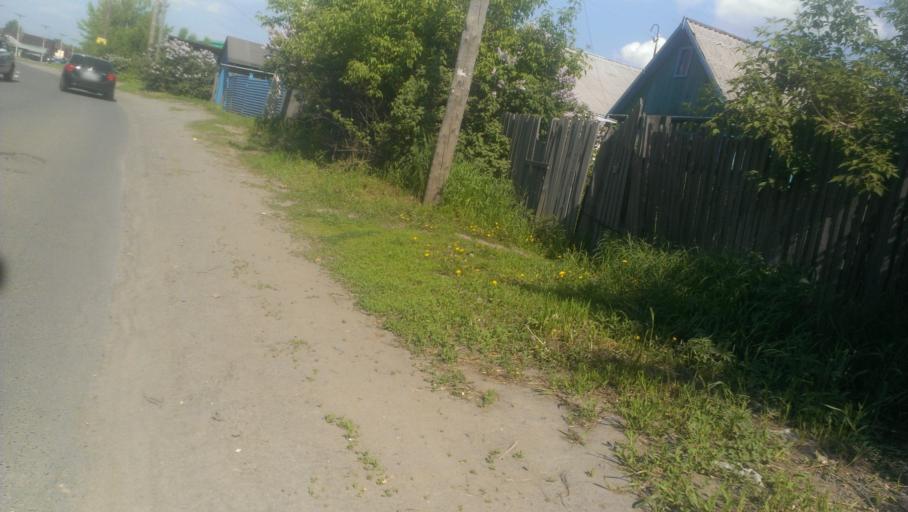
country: RU
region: Altai Krai
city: Novoaltaysk
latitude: 53.3999
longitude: 83.9396
